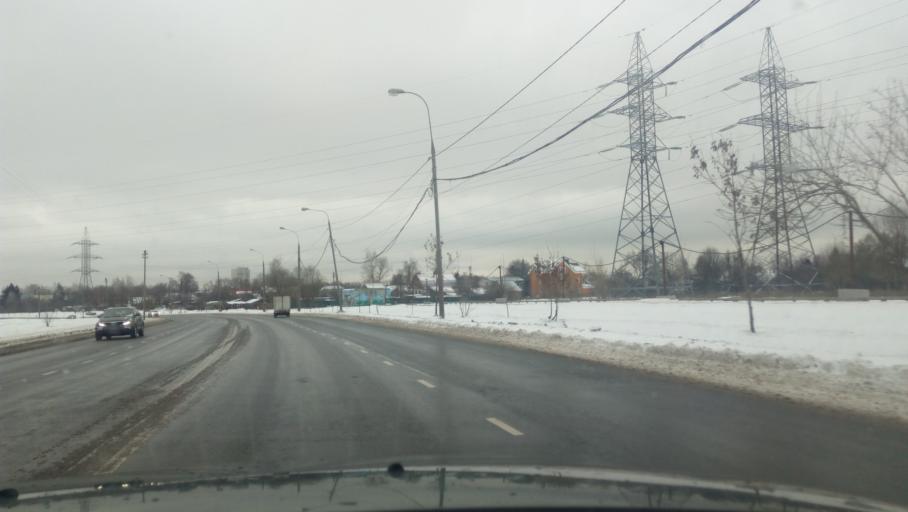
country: RU
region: Moscow
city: Zhulebino
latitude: 55.7249
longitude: 37.8586
